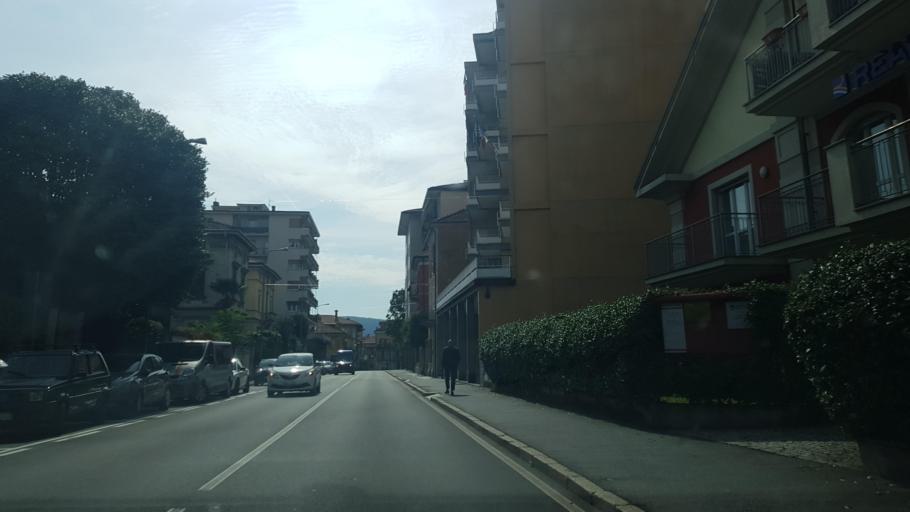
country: IT
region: Piedmont
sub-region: Provincia Verbano-Cusio-Ossola
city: Verbania
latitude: 45.9247
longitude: 8.5517
